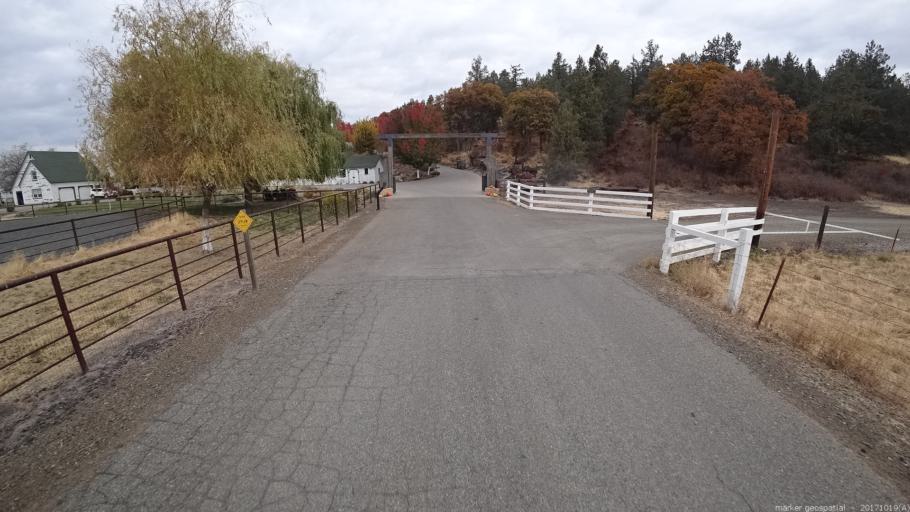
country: US
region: California
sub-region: Shasta County
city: Burney
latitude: 41.0915
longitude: -121.3654
